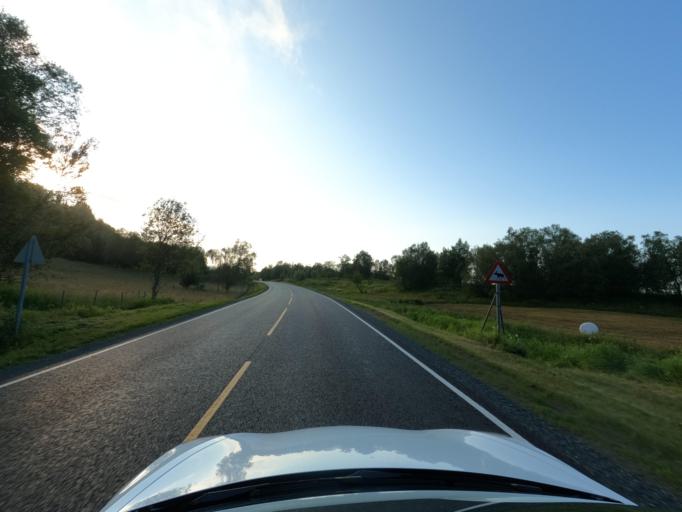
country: NO
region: Troms
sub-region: Skanland
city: Evenskjer
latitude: 68.6738
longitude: 16.5682
